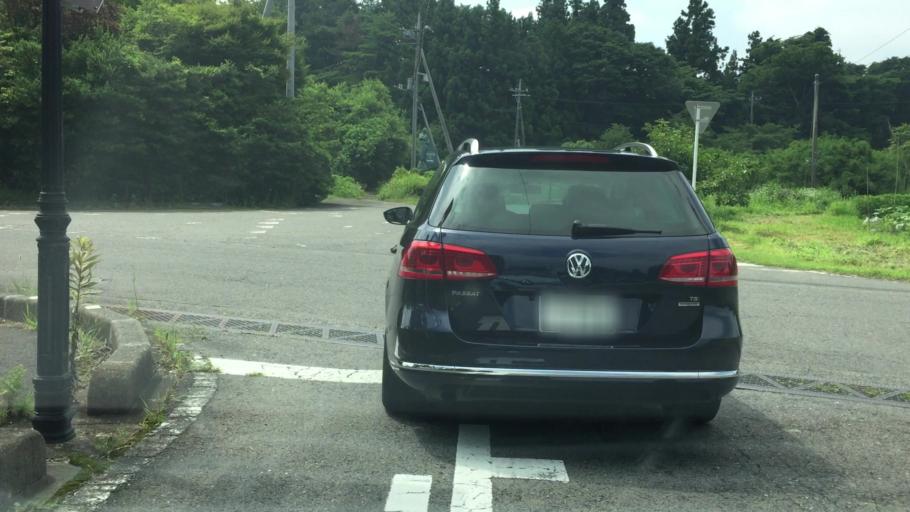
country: JP
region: Tochigi
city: Kuroiso
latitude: 37.0476
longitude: 140.0290
